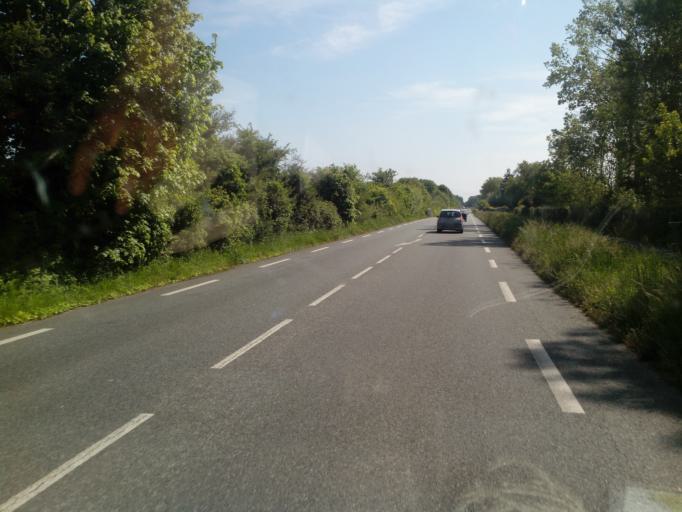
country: FR
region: Nord-Pas-de-Calais
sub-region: Departement du Pas-de-Calais
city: Verton
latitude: 50.3618
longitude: 1.6524
